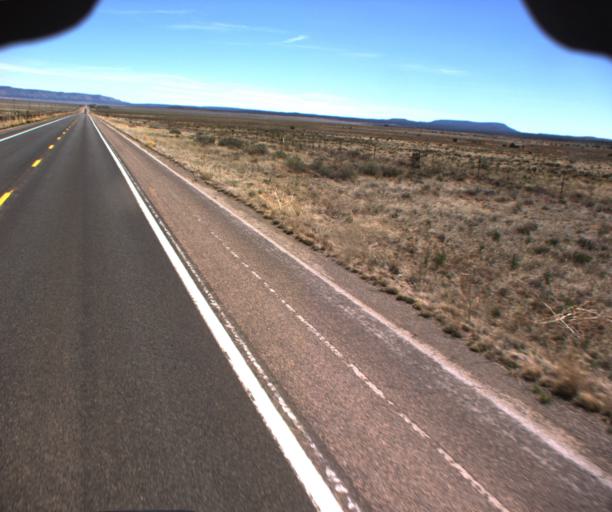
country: US
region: Arizona
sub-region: Mohave County
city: Peach Springs
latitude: 35.4913
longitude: -113.1581
